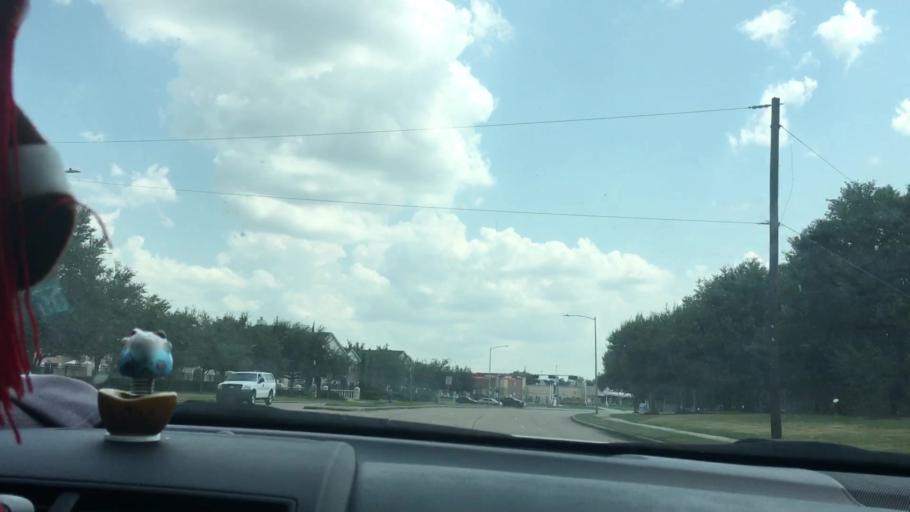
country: US
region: Texas
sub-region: Fort Bend County
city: Mission Bend
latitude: 29.7308
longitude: -95.6363
